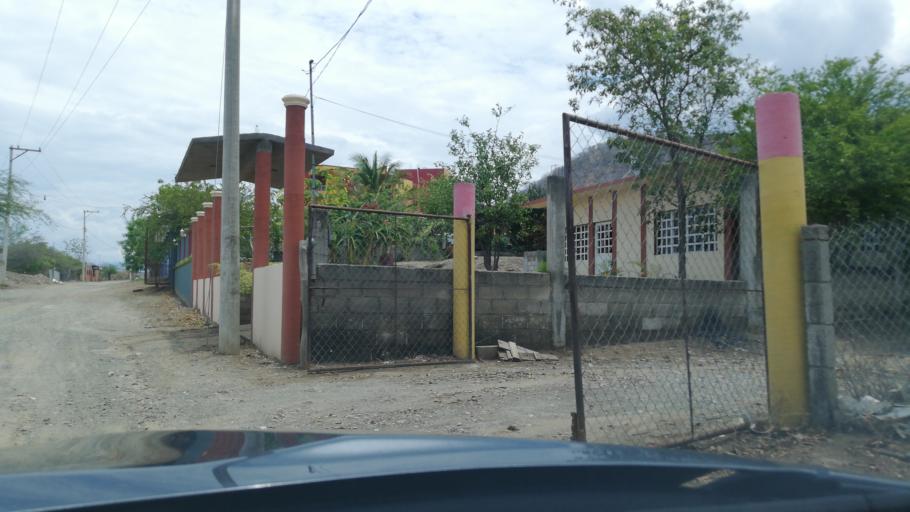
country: MX
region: Oaxaca
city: Santa Maria Jalapa del Marques
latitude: 16.4488
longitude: -95.4424
